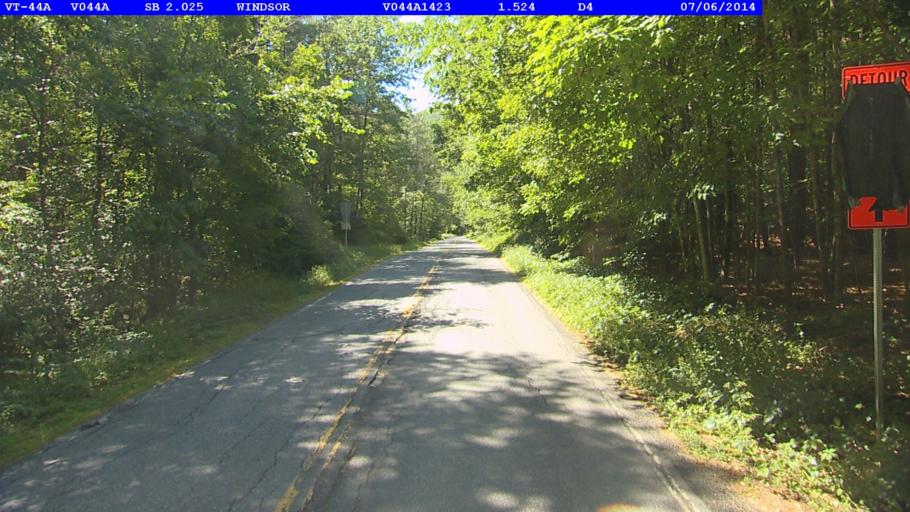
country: US
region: Vermont
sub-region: Windsor County
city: Windsor
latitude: 43.4473
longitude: -72.4155
